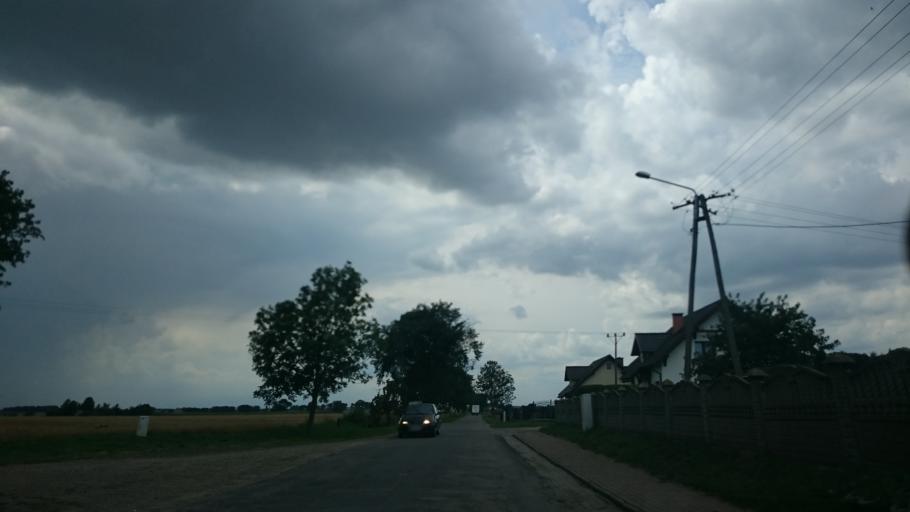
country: PL
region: Pomeranian Voivodeship
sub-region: Powiat chojnicki
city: Chojnice
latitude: 53.6690
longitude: 17.6689
